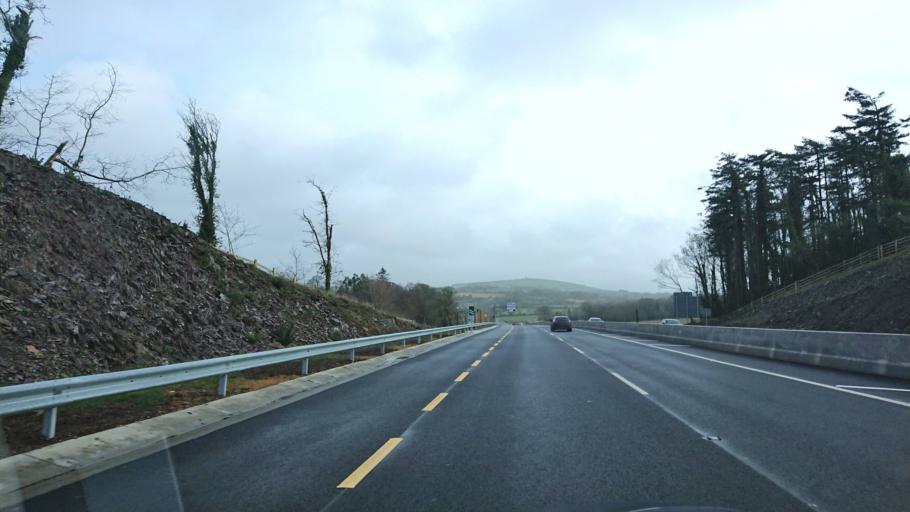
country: IE
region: Leinster
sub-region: Loch Garman
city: New Ross
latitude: 52.3607
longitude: -6.9711
